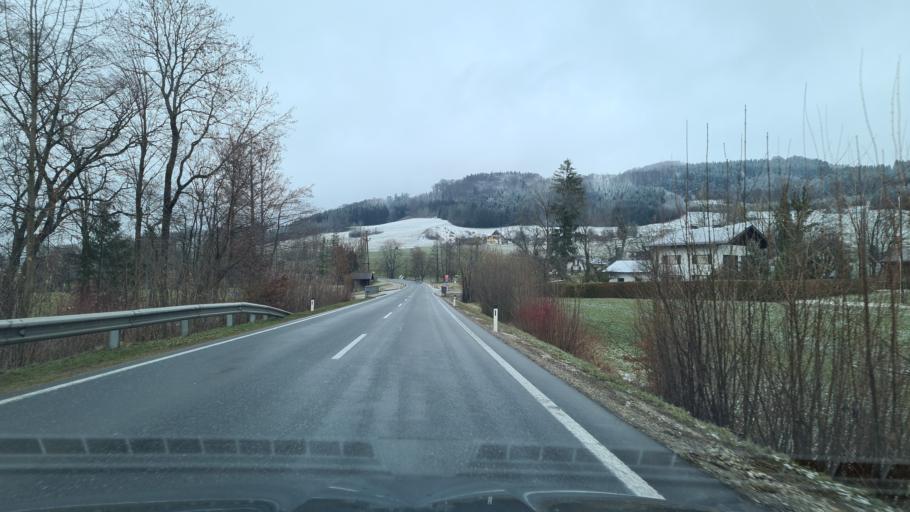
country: AT
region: Upper Austria
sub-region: Politischer Bezirk Vocklabruck
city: Zell am Moos
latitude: 47.9158
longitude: 13.3155
